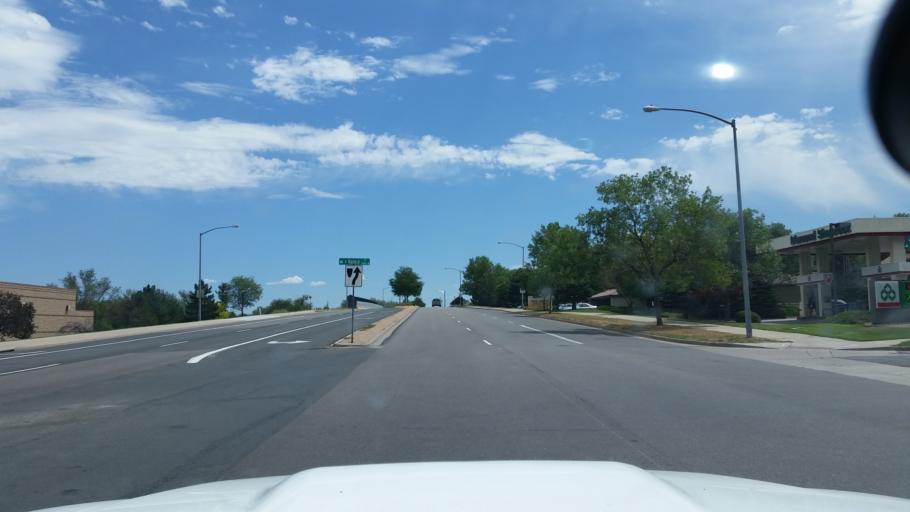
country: US
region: Colorado
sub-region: Adams County
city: Westminster
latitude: 39.8636
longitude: -105.0801
